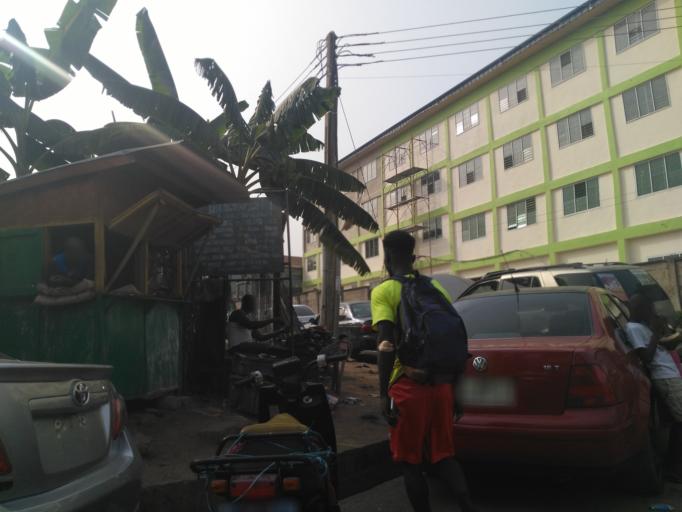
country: GH
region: Ashanti
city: Kumasi
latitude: 6.6878
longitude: -1.6084
